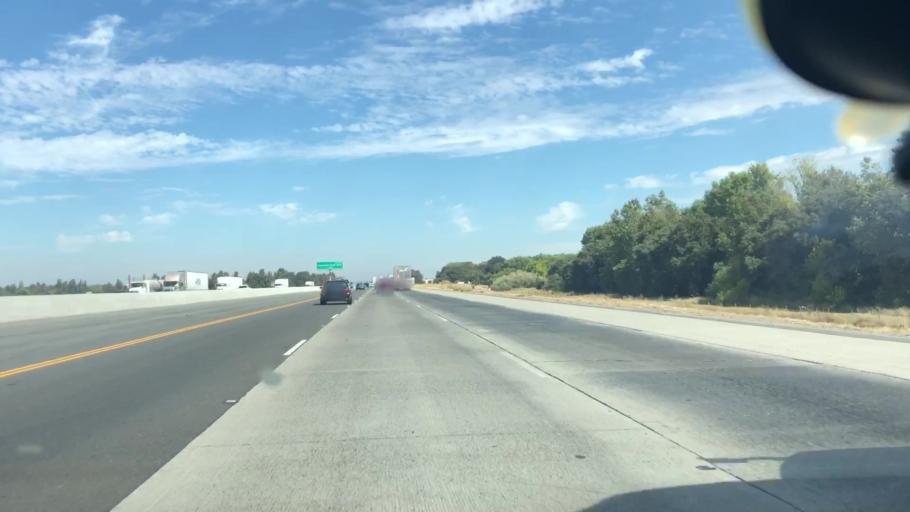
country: US
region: California
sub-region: Sacramento County
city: Parkway
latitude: 38.4447
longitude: -121.4902
